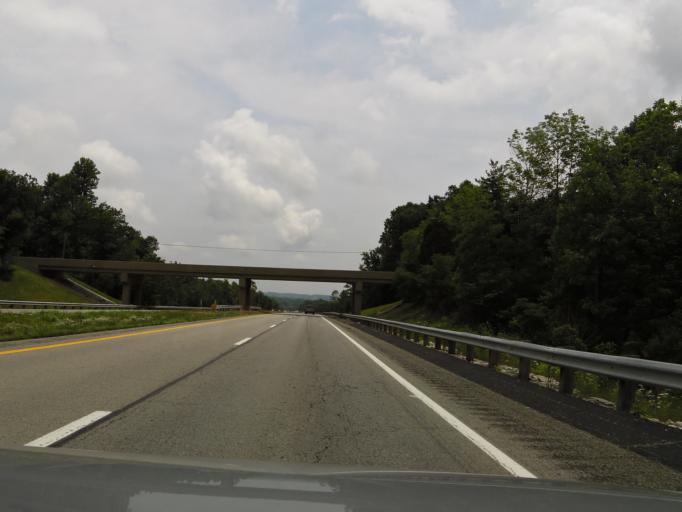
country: US
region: Kentucky
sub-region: Grayson County
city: Leitchfield
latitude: 37.5563
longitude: -86.0797
